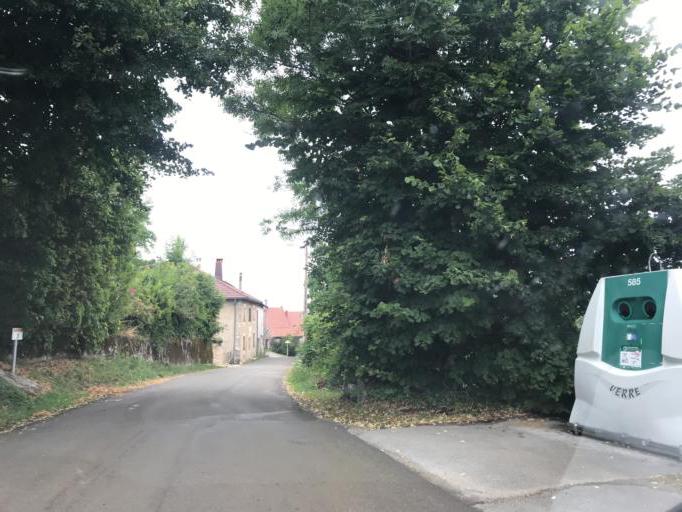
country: FR
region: Franche-Comte
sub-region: Departement du Jura
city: Lavans-les-Saint-Claude
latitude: 46.3250
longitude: 5.7470
